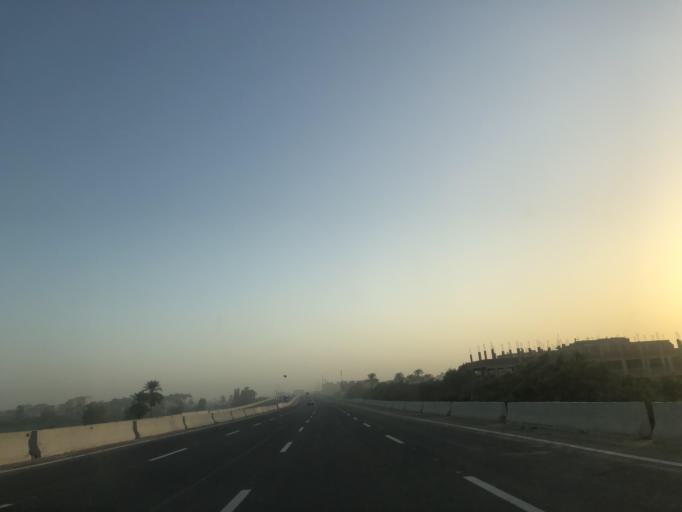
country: EG
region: Al Jizah
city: Al Jizah
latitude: 29.9531
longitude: 31.1483
